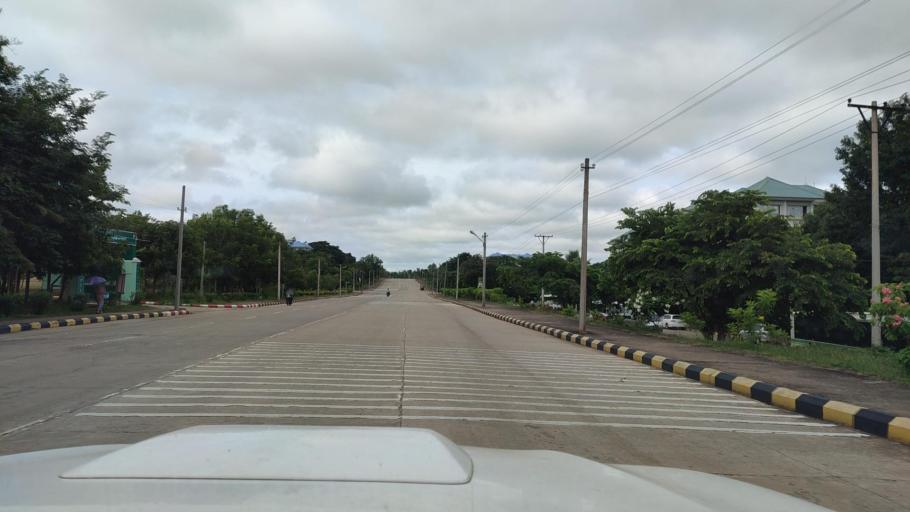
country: MM
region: Mandalay
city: Nay Pyi Taw
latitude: 19.7385
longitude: 96.0598
